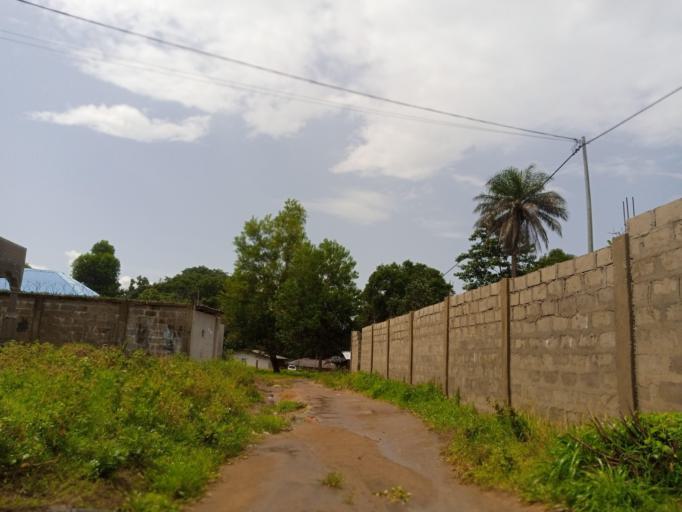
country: SL
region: Northern Province
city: Sawkta
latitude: 8.6323
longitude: -13.2032
